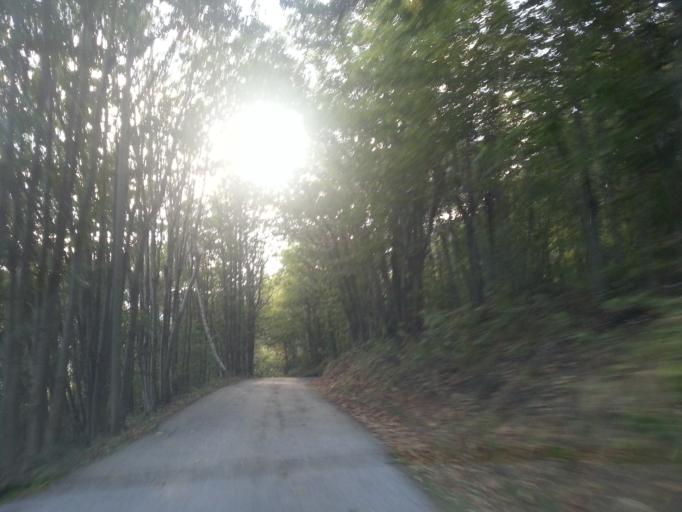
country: IT
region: Lombardy
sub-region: Provincia di Como
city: Sorico
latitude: 46.1849
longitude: 9.3906
